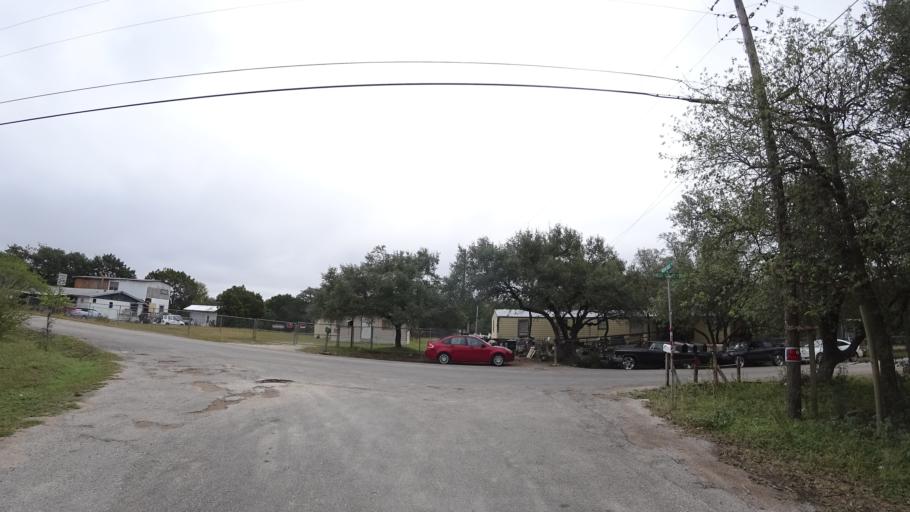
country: US
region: Texas
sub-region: Travis County
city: Shady Hollow
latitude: 30.2218
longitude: -97.8964
